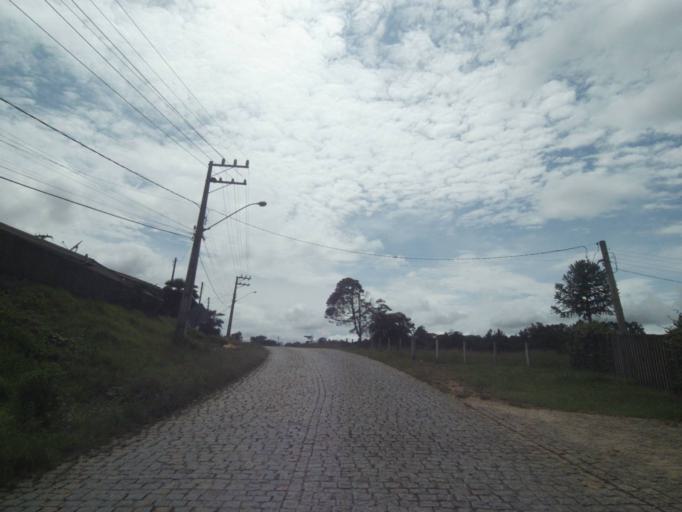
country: BR
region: Parana
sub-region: Campina Grande Do Sul
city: Campina Grande do Sul
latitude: -25.3072
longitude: -49.0465
